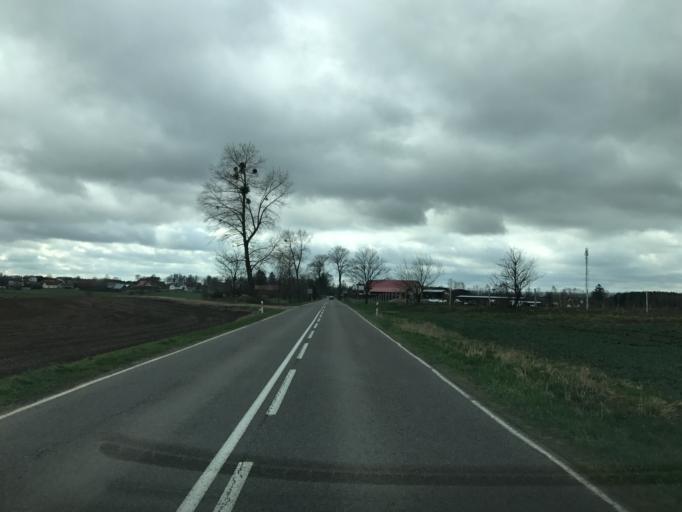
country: PL
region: Warmian-Masurian Voivodeship
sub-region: Powiat ostrodzki
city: Gierzwald
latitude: 53.4973
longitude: 20.1466
